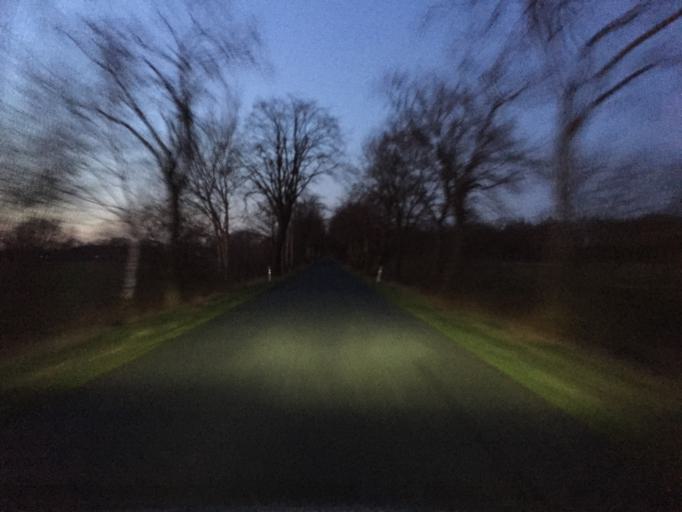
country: DE
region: Lower Saxony
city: Sulingen
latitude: 52.6531
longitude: 8.8155
